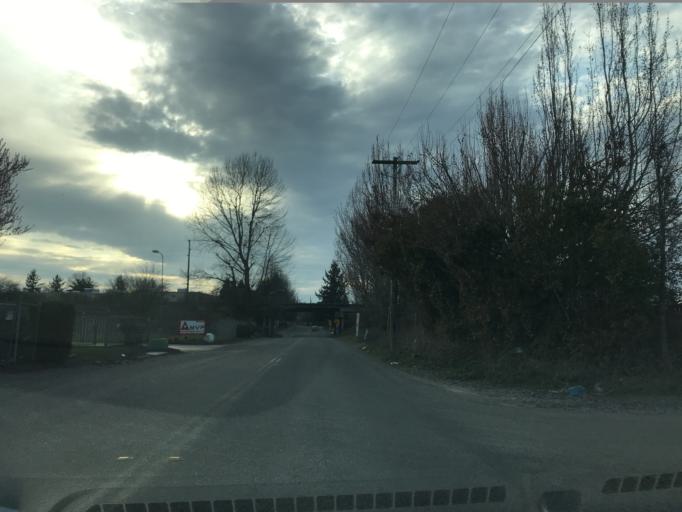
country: US
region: Washington
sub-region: King County
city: Kent
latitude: 47.3633
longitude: -122.2315
